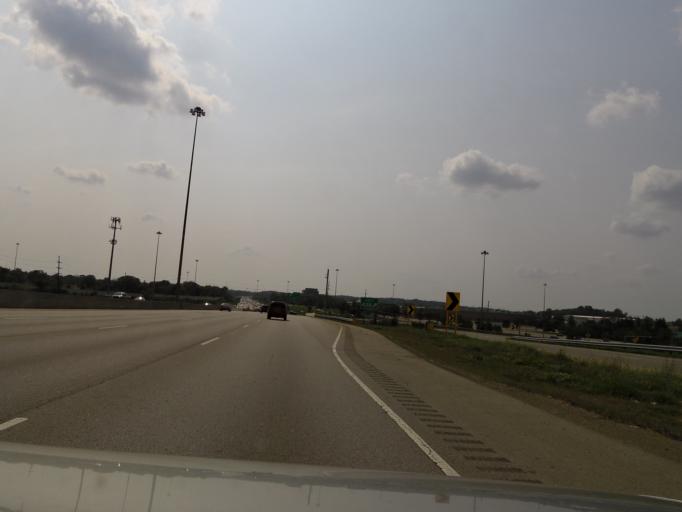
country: US
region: Ohio
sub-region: Hamilton County
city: Springdale
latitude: 39.2948
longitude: -84.4641
